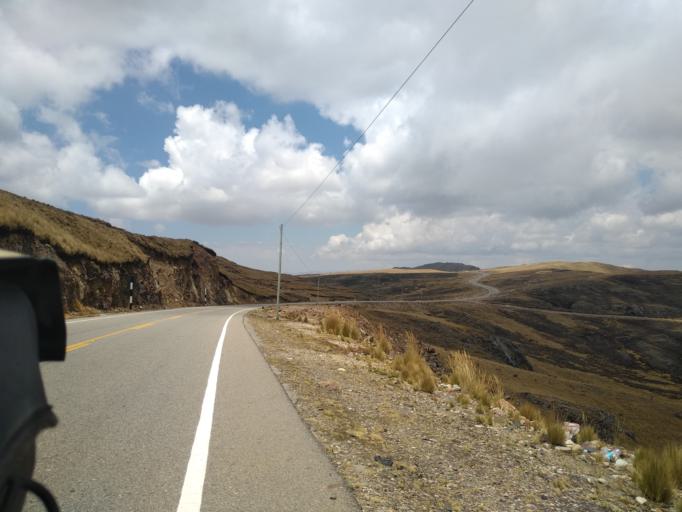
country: PE
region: La Libertad
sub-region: Provincia de Santiago de Chuco
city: Quiruvilca
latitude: -7.9580
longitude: -78.1957
